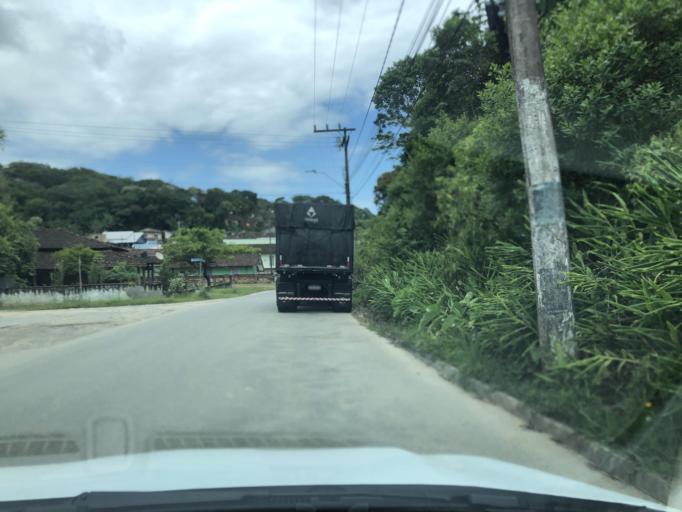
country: BR
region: Santa Catarina
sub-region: Sao Francisco Do Sul
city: Sao Francisco do Sul
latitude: -26.2305
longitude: -48.6073
